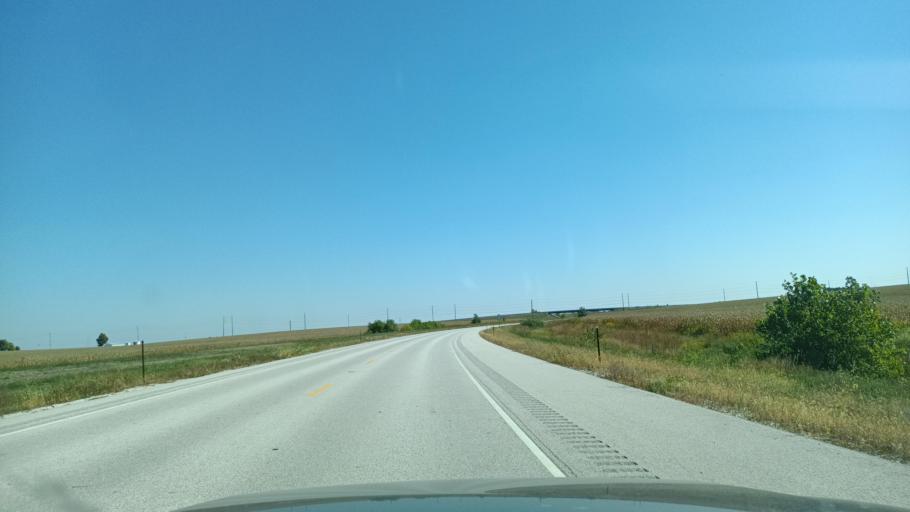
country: US
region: Illinois
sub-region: McDonough County
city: Macomb
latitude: 40.5025
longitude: -90.7026
